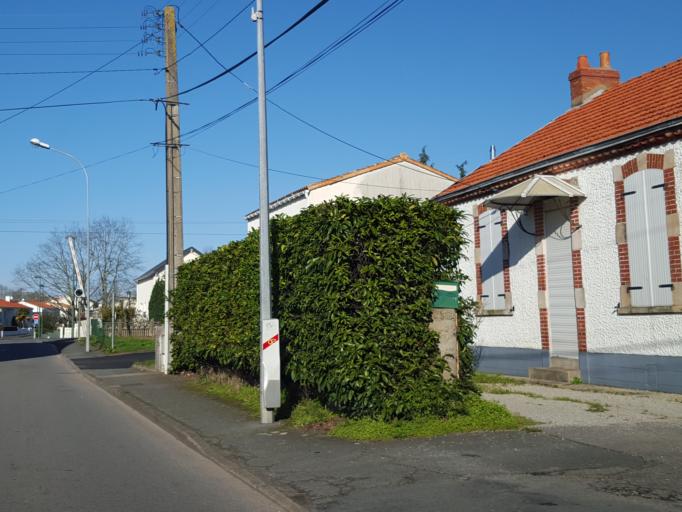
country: FR
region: Pays de la Loire
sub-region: Departement de la Vendee
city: La Roche-sur-Yon
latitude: 46.6594
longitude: -1.4504
